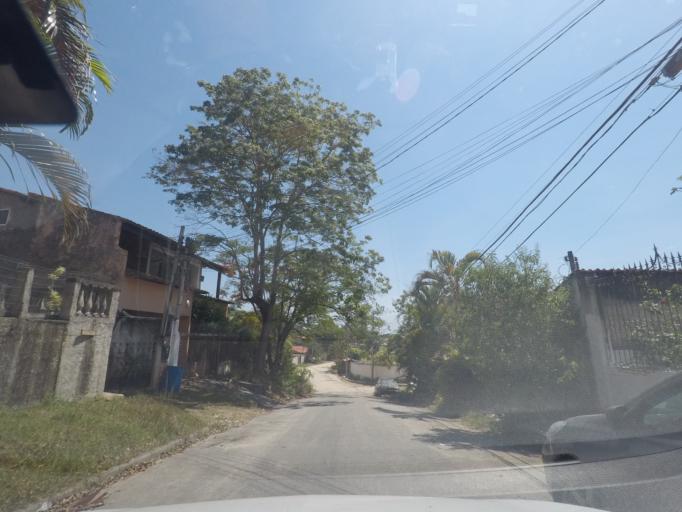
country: BR
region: Rio de Janeiro
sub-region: Niteroi
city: Niteroi
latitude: -22.9335
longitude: -43.0145
